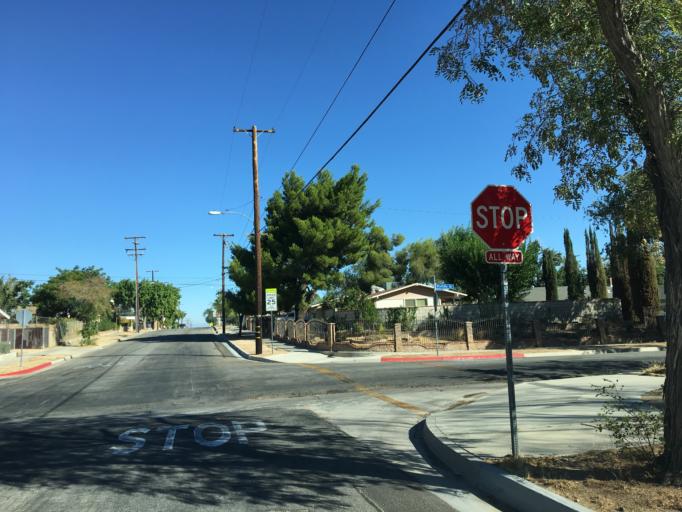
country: US
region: California
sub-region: Los Angeles County
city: Desert View Highlands
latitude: 34.5915
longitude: -118.1527
